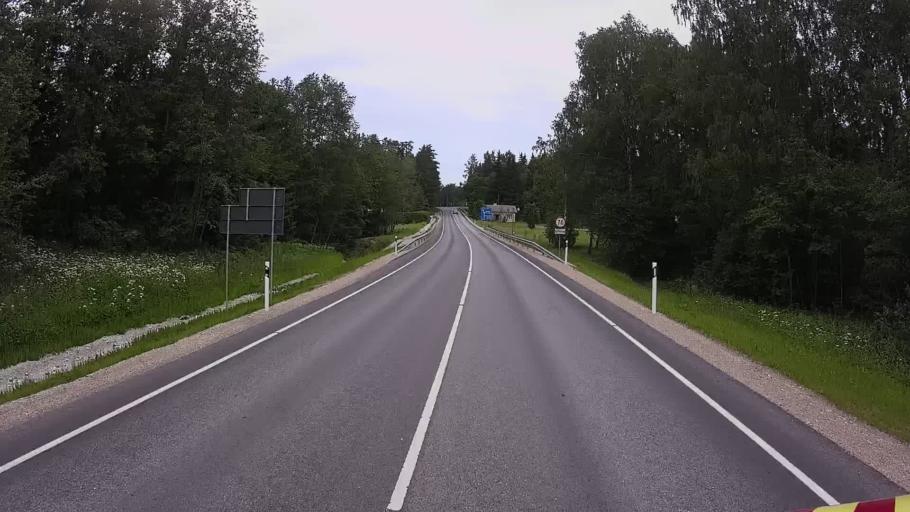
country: EE
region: Viljandimaa
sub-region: Viljandi linn
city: Viljandi
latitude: 58.2813
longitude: 25.5838
